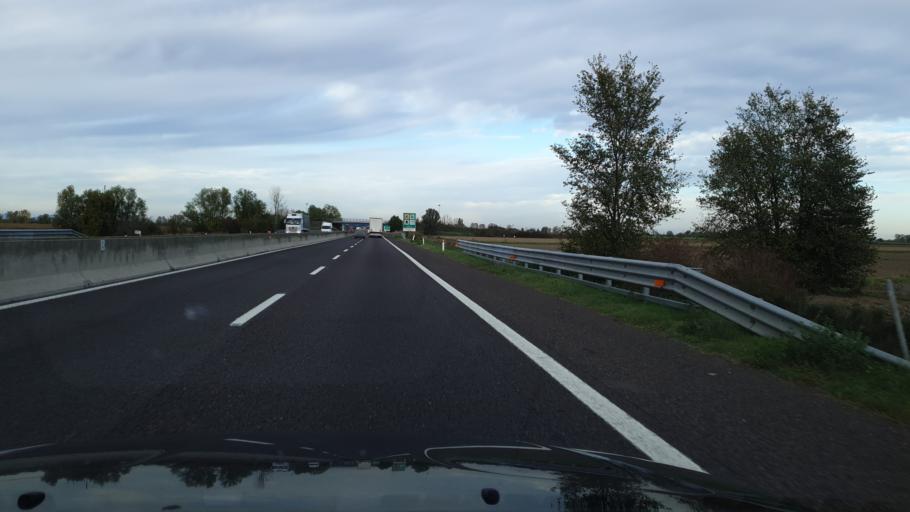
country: IT
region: Veneto
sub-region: Provincia di Rovigo
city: Costa di Rovigo
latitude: 45.0353
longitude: 11.7053
